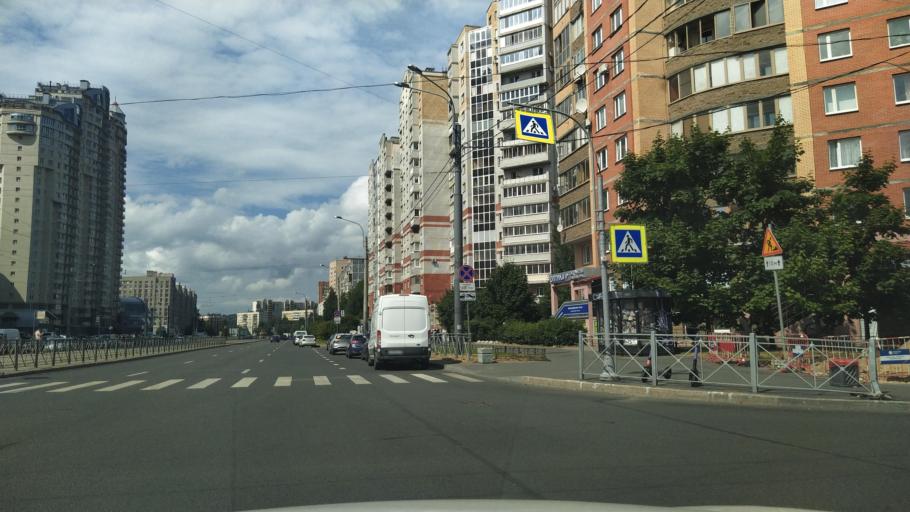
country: RU
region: St.-Petersburg
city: Ozerki
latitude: 60.0426
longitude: 30.3348
